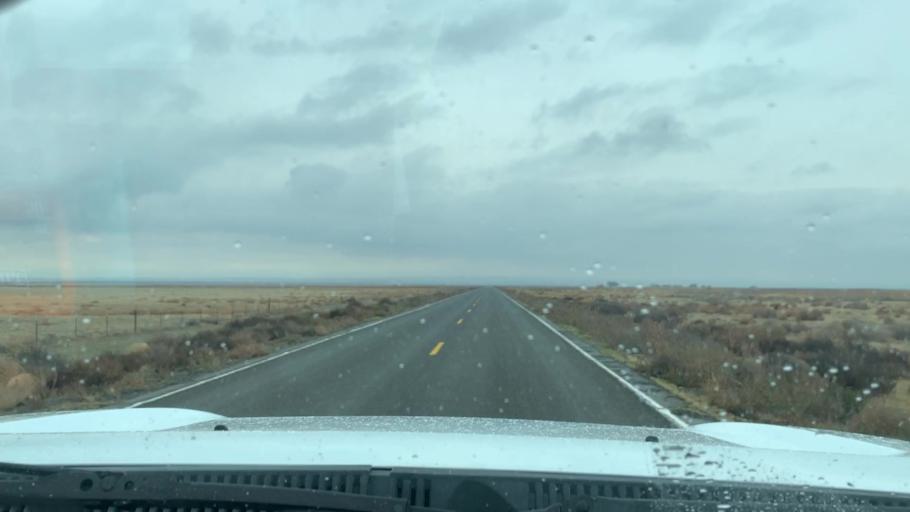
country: US
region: California
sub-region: Kings County
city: Kettleman City
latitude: 35.9341
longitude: -119.7843
